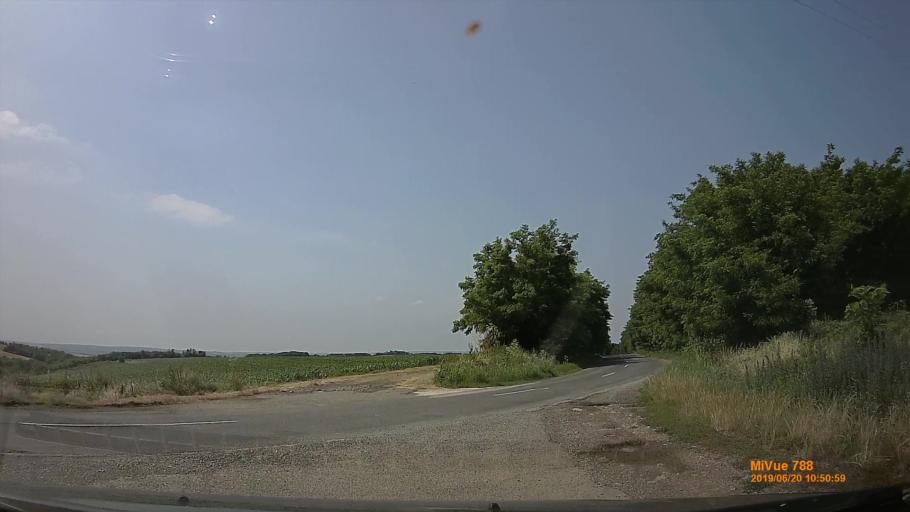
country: HU
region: Baranya
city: Mecseknadasd
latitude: 46.1583
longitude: 18.5814
